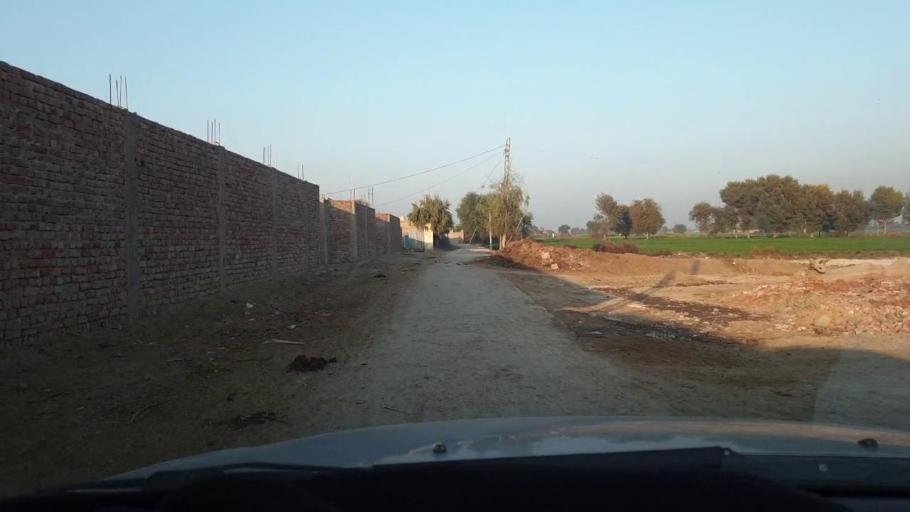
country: PK
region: Sindh
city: Mirpur Mathelo
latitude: 27.9982
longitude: 69.6057
